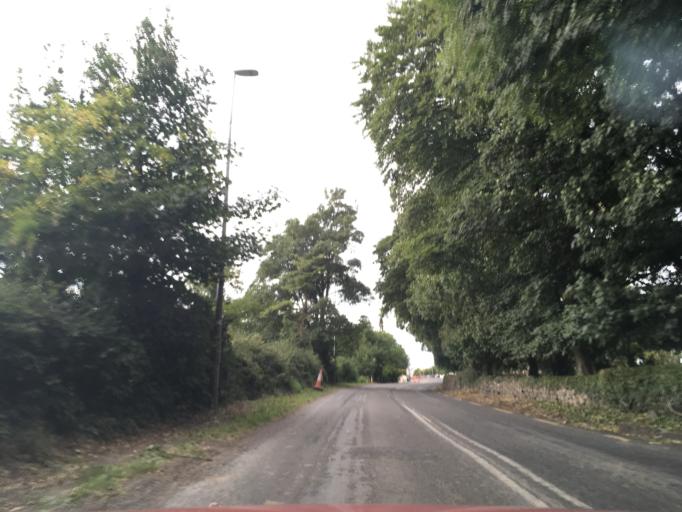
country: IE
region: Munster
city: Cahir
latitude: 52.4374
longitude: -7.8836
